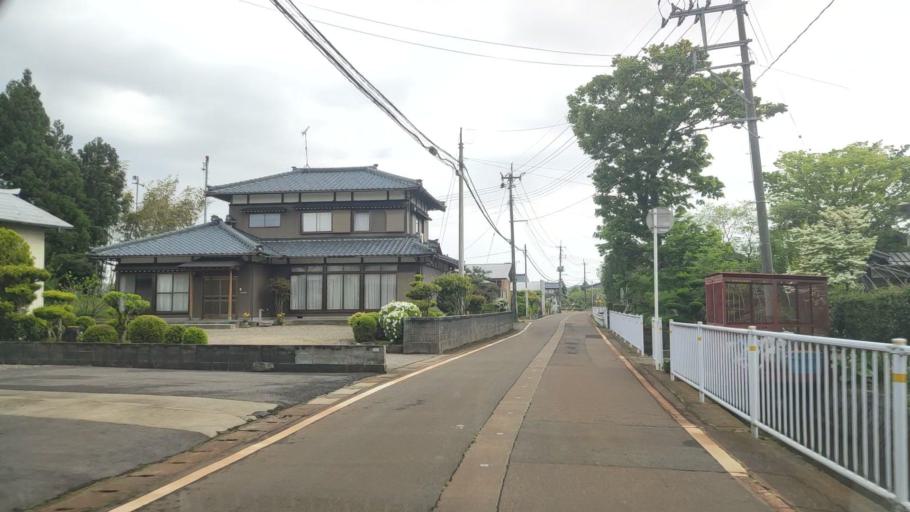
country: JP
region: Niigata
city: Gosen
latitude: 37.7310
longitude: 139.1620
